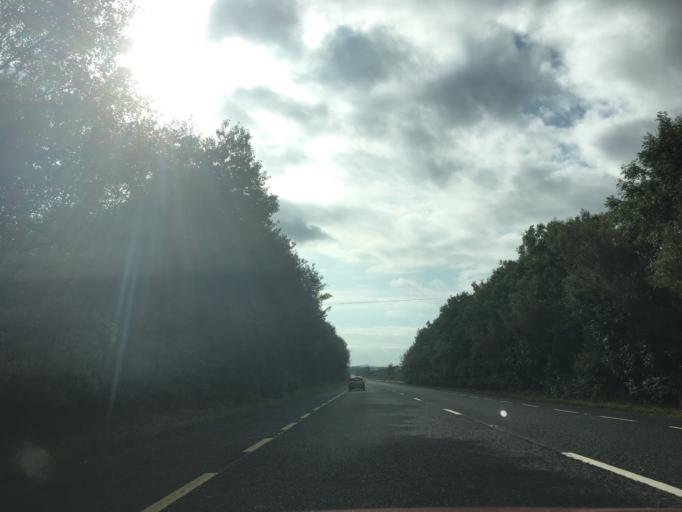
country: IE
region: Leinster
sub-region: Loch Garman
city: Loch Garman
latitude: 52.3459
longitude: -6.5994
